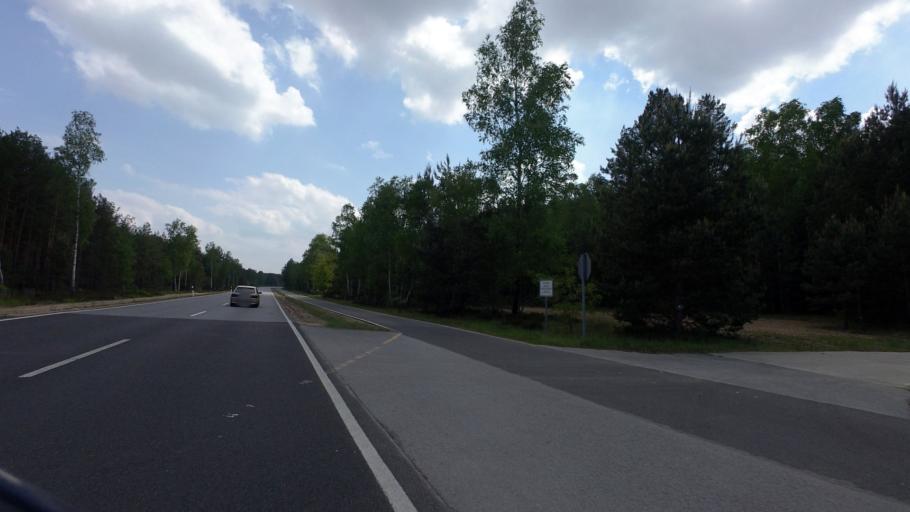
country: DE
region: Saxony
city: Rietschen
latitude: 51.4405
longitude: 14.7806
